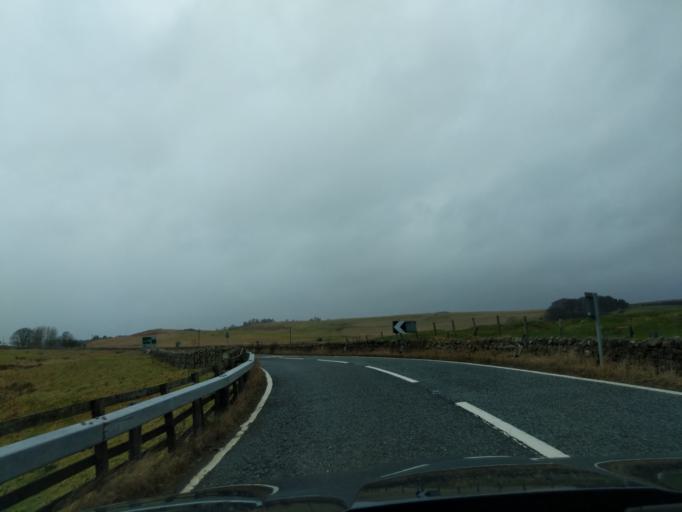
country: GB
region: England
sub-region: Northumberland
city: Otterburn
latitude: 55.2270
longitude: -2.1565
